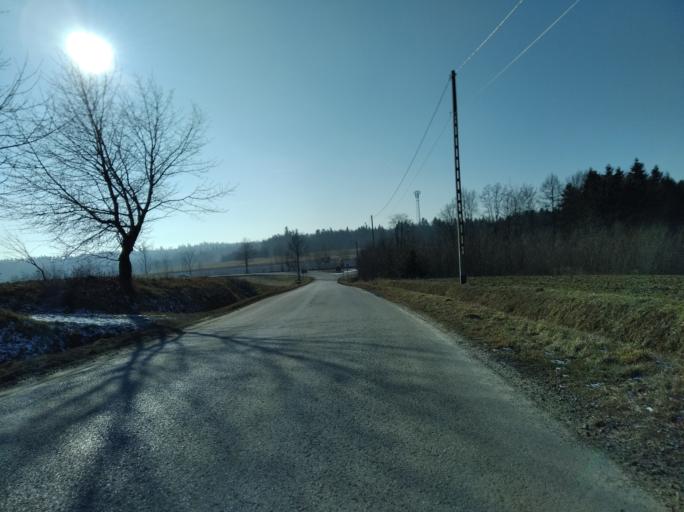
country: PL
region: Subcarpathian Voivodeship
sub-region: Powiat rzeszowski
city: Straszydle
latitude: 49.8789
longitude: 21.9849
